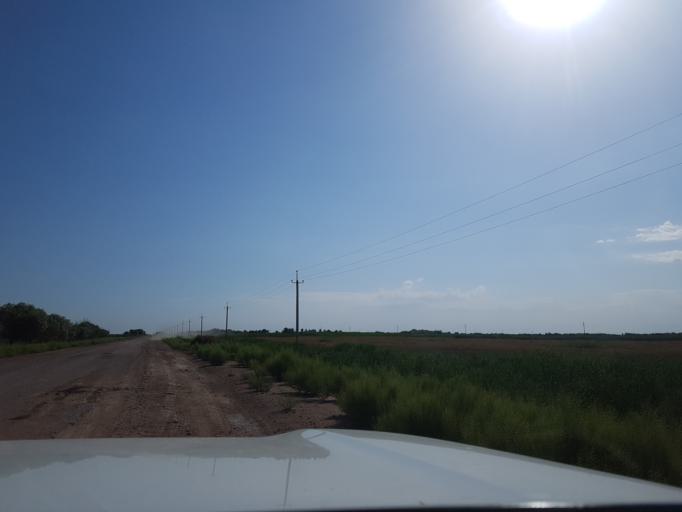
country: TM
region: Dasoguz
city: Koeneuergench
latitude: 42.0387
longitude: 58.8135
